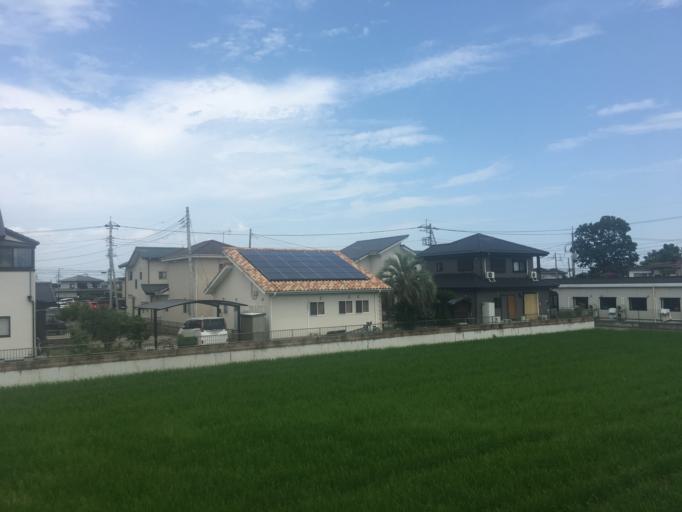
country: JP
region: Gunma
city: Fujioka
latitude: 36.2793
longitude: 139.0837
